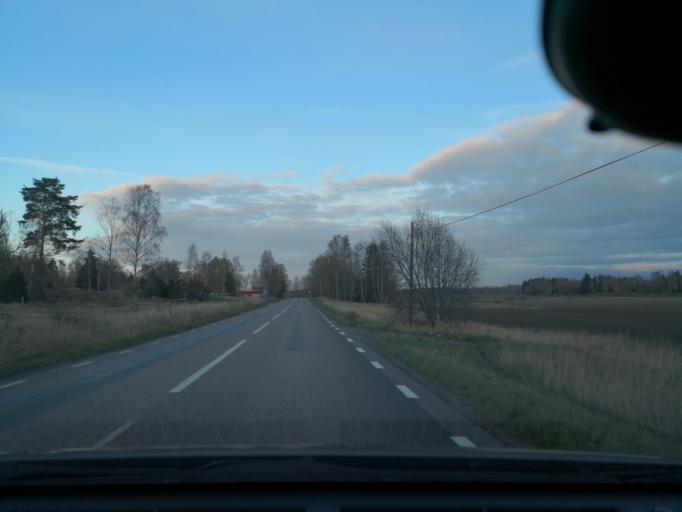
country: SE
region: Vaestmanland
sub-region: Vasteras
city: Tillberga
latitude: 59.6383
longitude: 16.6738
